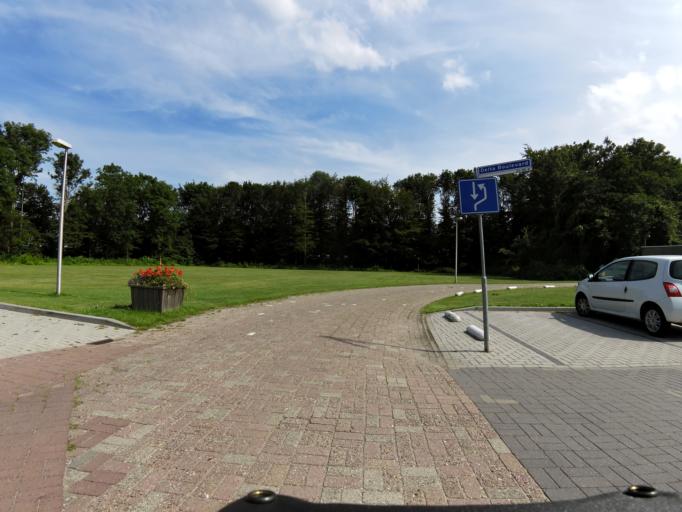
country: NL
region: South Holland
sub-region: Gemeente Goeree-Overflakkee
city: Middelharnis
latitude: 51.7608
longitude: 4.1823
